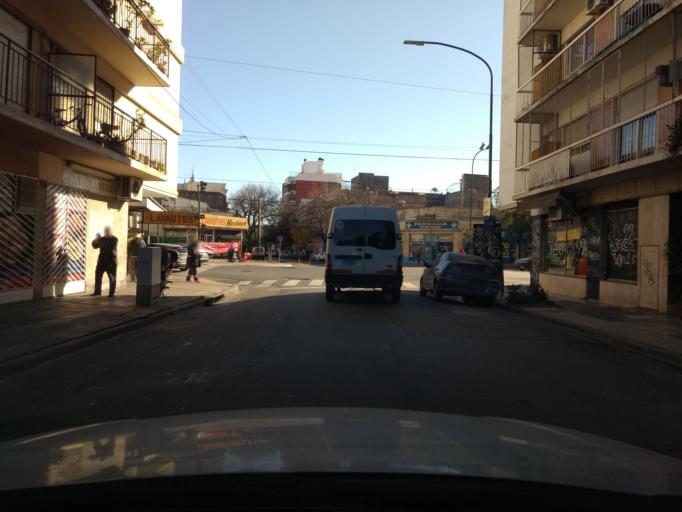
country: AR
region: Buenos Aires F.D.
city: Villa Santa Rita
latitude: -34.6181
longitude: -58.4690
